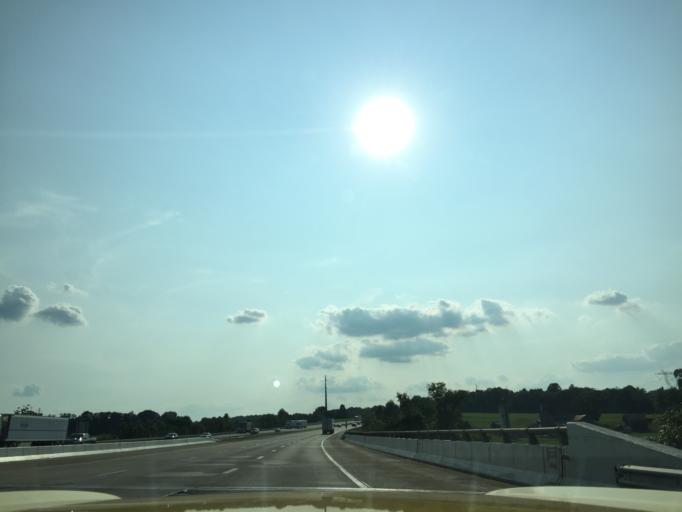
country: US
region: Maryland
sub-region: Cecil County
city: Elkton
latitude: 39.6420
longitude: -75.8659
